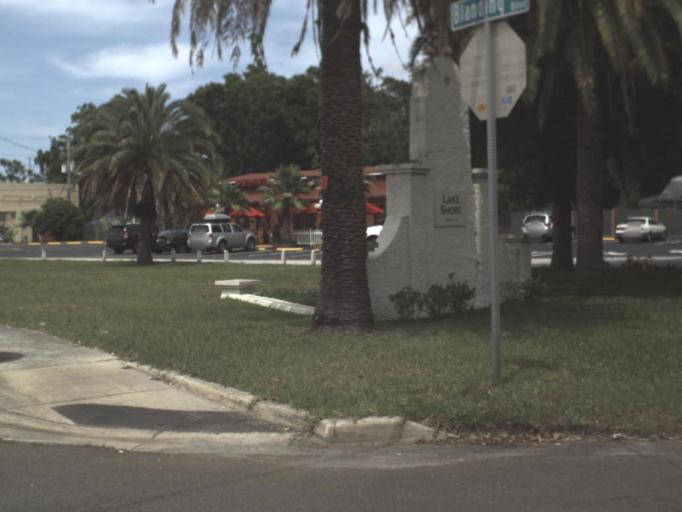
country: US
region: Florida
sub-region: Duval County
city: Jacksonville
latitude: 30.2805
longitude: -81.7265
